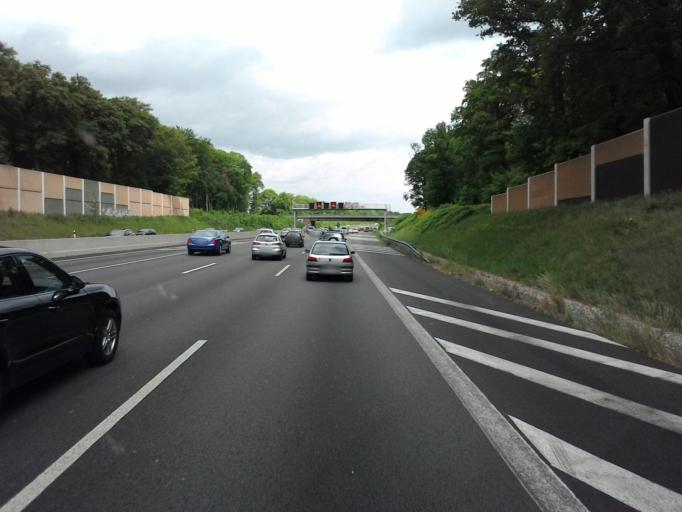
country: DE
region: North Rhine-Westphalia
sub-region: Regierungsbezirk Koln
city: Muelheim
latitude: 50.9886
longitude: 7.0133
